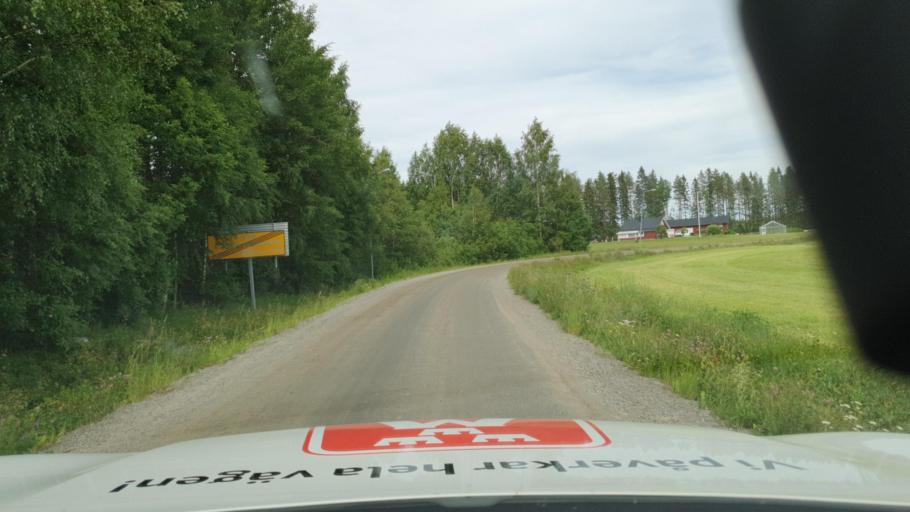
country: SE
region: Vaesterbotten
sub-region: Skelleftea Kommun
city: Viken
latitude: 64.4994
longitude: 20.9114
